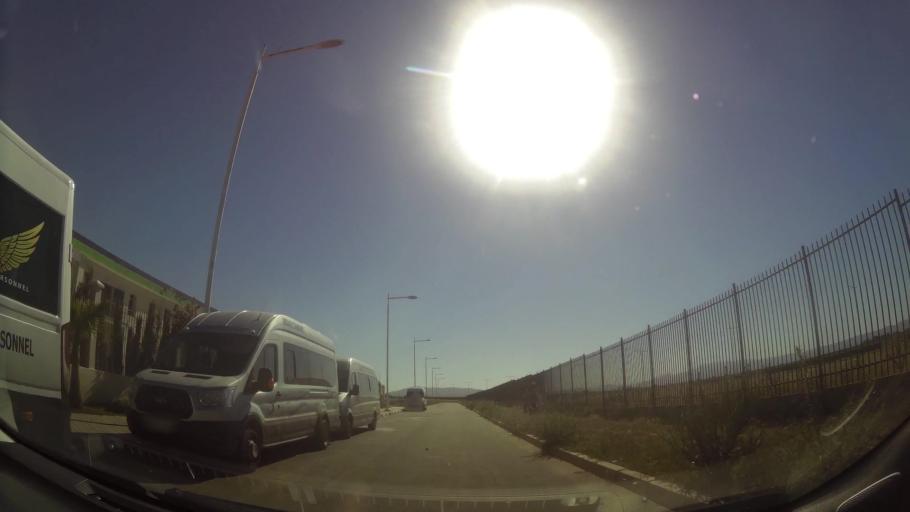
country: MA
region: Oriental
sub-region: Oujda-Angad
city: Oujda
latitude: 34.7758
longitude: -1.9339
